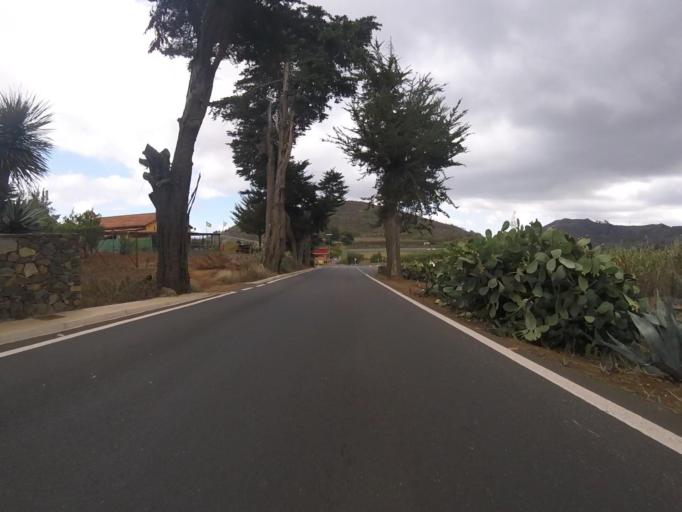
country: ES
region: Canary Islands
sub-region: Provincia de Las Palmas
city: Vega de San Mateo
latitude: 28.0088
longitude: -15.5448
